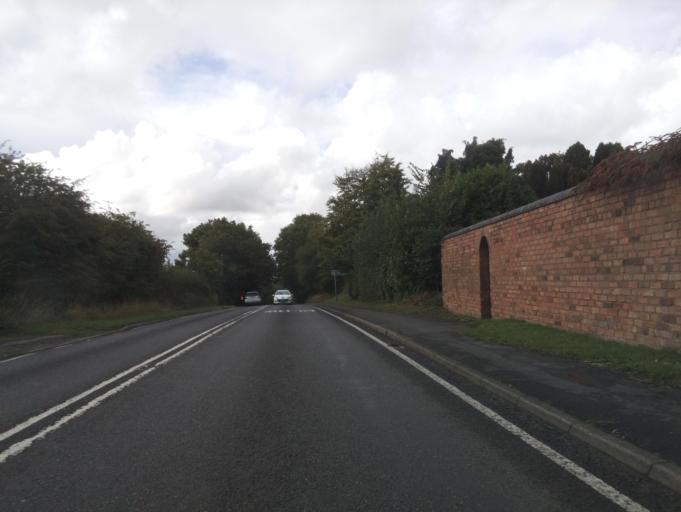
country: GB
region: England
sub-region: Worcestershire
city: Kidderminster
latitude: 52.3726
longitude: -2.2056
